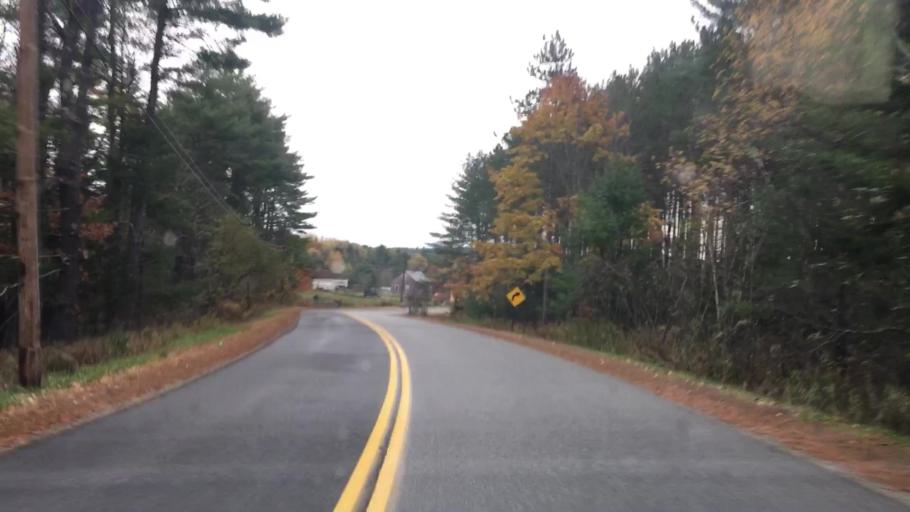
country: US
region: Maine
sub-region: Lincoln County
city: Whitefield
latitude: 44.1664
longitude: -69.6943
